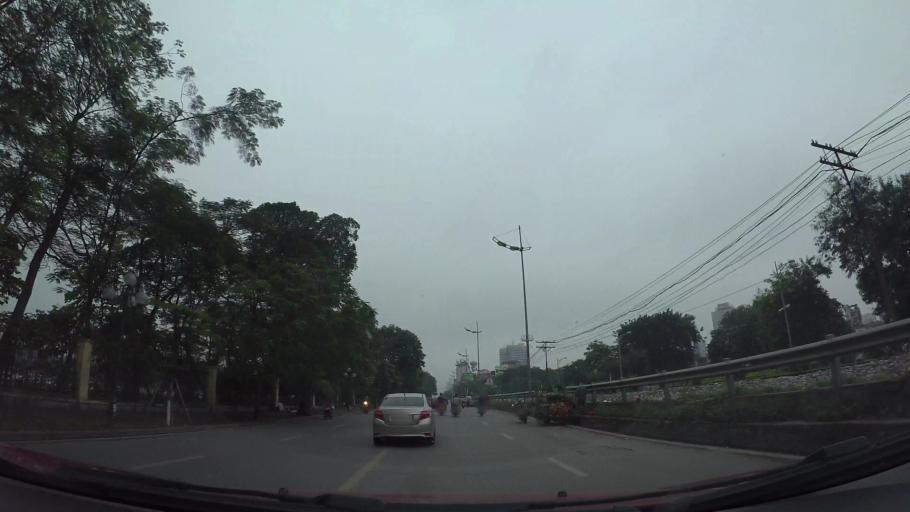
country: VN
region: Ha Noi
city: Hai BaTrung
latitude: 21.0129
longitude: 105.8413
